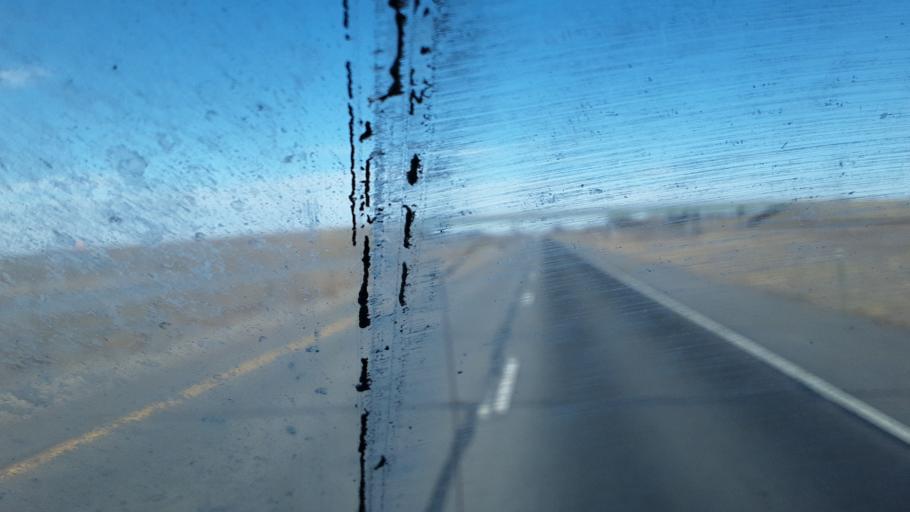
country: US
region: Colorado
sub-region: Weld County
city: Lochbuie
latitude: 40.0131
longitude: -104.7011
